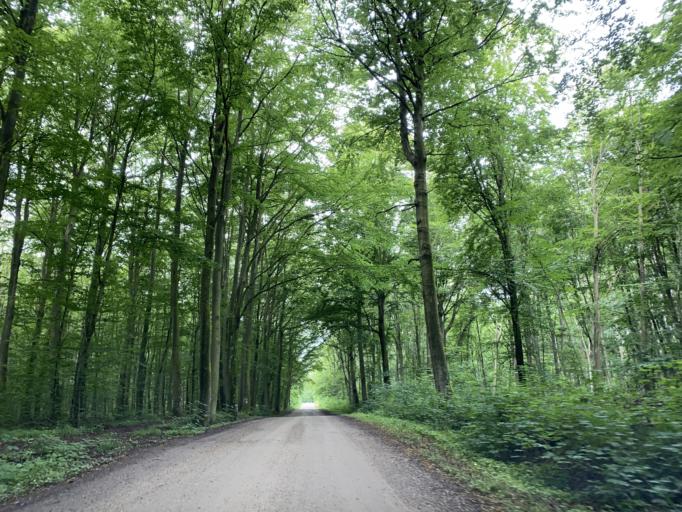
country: DK
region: South Denmark
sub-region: Sonderborg Kommune
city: Sonderborg
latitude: 54.9028
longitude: 9.8324
